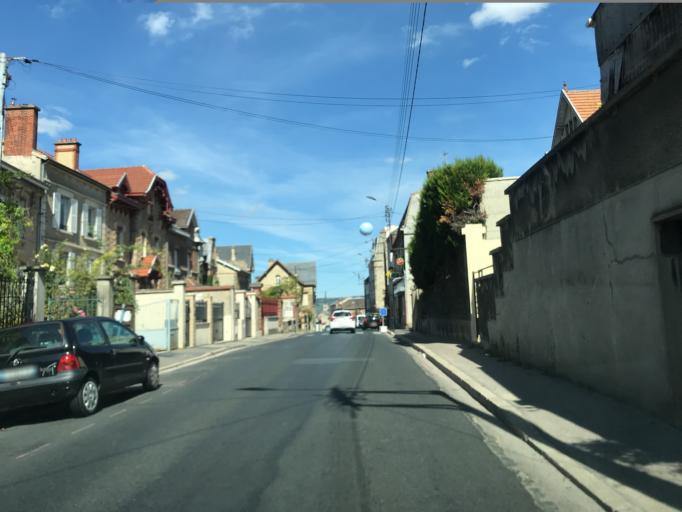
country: FR
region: Champagne-Ardenne
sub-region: Departement de la Marne
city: Epernay
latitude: 49.0340
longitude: 3.9535
